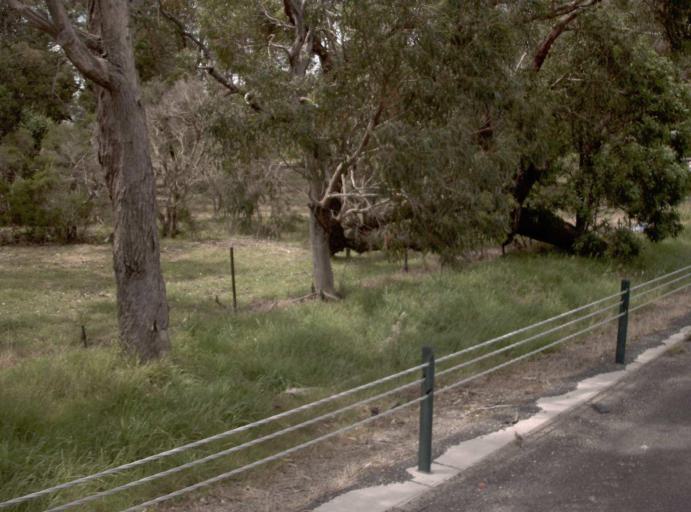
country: AU
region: Victoria
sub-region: Mornington Peninsula
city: Tyabb
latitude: -38.2284
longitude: 145.2169
